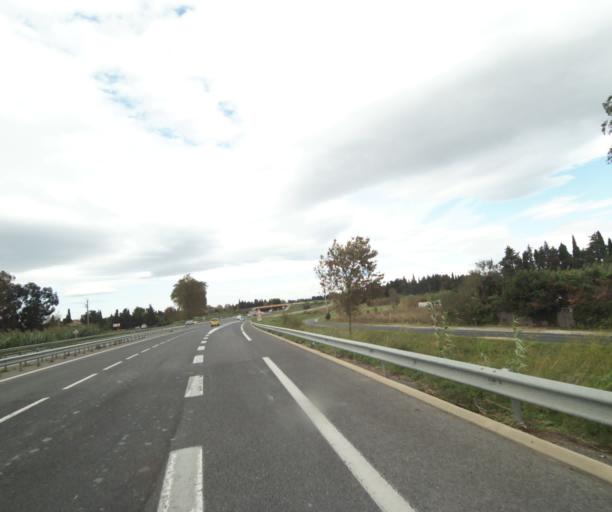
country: FR
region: Languedoc-Roussillon
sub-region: Departement des Pyrenees-Orientales
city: Elne
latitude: 42.5868
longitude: 2.9841
